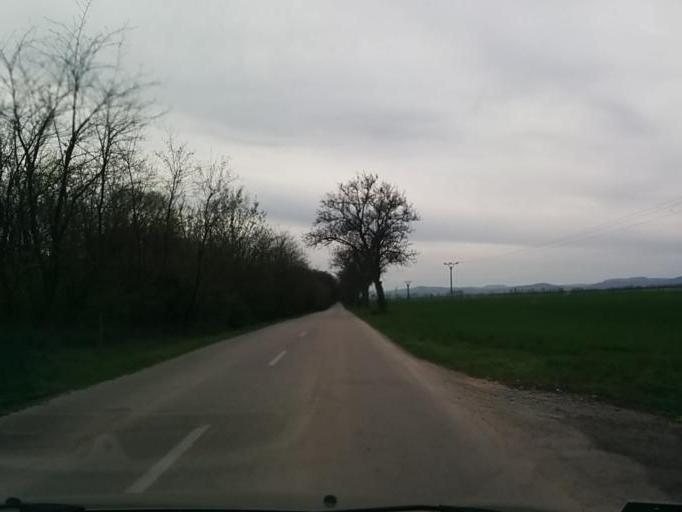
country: SK
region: Trnavsky
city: Sladkovicovo
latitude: 48.2464
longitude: 17.5351
